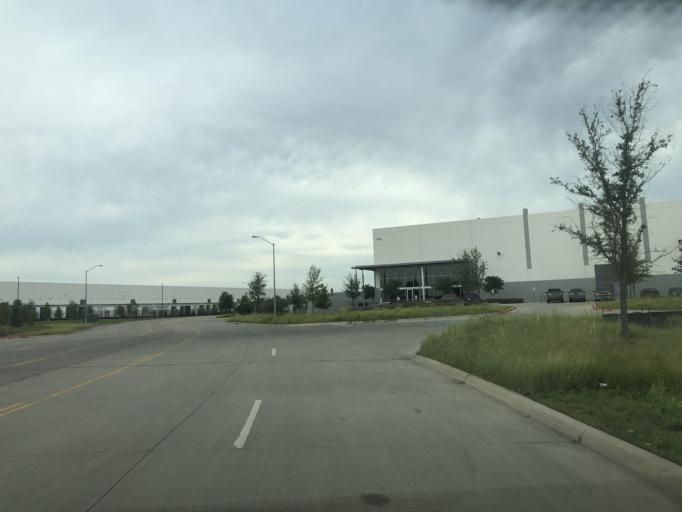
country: US
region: Texas
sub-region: Dallas County
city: Grand Prairie
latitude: 32.7729
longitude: -96.9958
